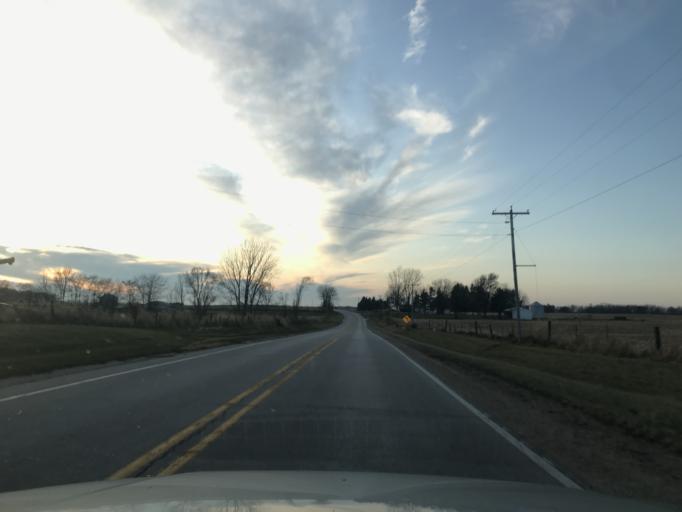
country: US
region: Illinois
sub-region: Warren County
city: Monmouth
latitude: 41.0250
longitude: -90.7716
